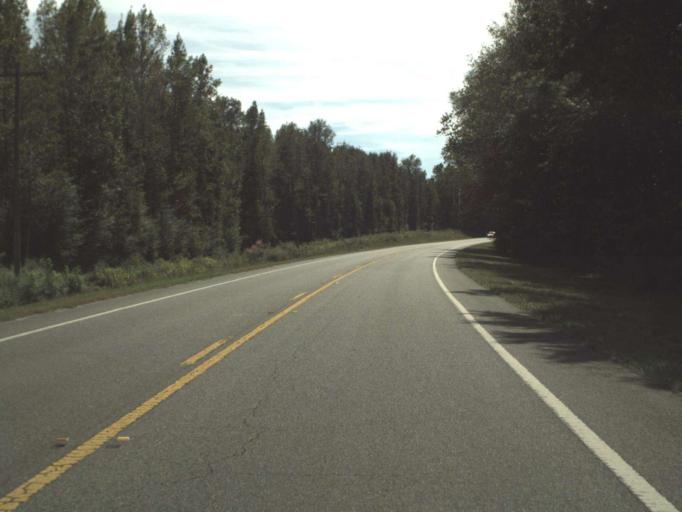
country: US
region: Florida
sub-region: Washington County
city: Chipley
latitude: 30.7254
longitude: -85.5538
